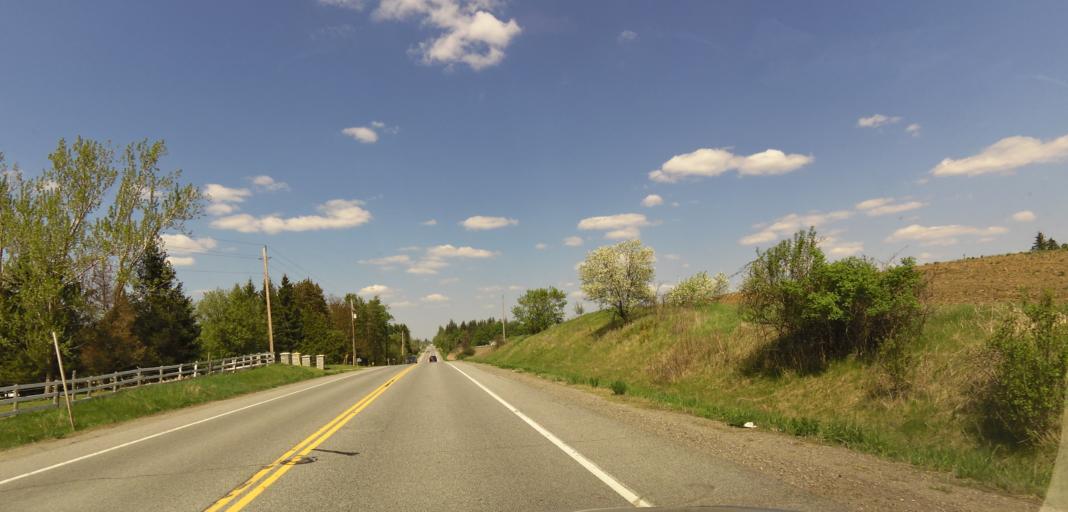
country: CA
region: Ontario
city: Brampton
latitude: 43.8353
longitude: -79.8770
